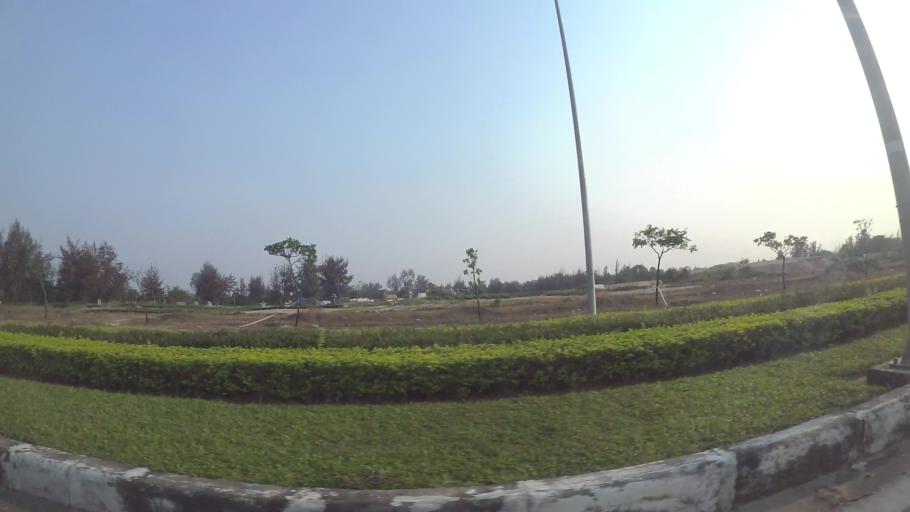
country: VN
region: Da Nang
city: Ngu Hanh Son
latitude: 15.9779
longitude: 108.2431
